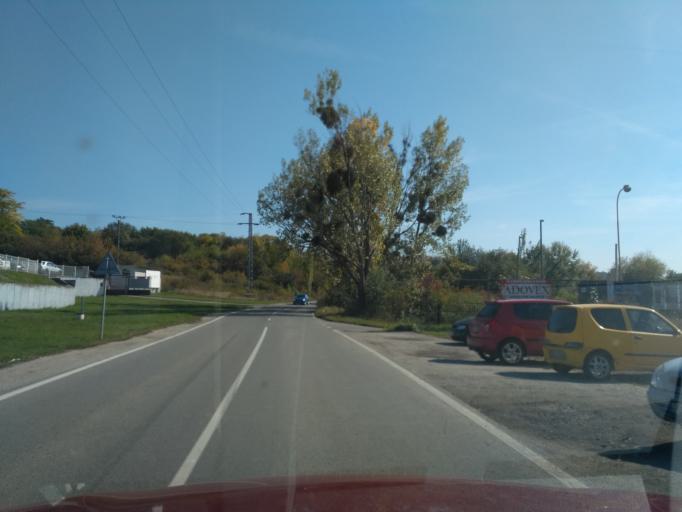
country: SK
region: Kosicky
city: Kosice
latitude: 48.7489
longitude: 21.2655
